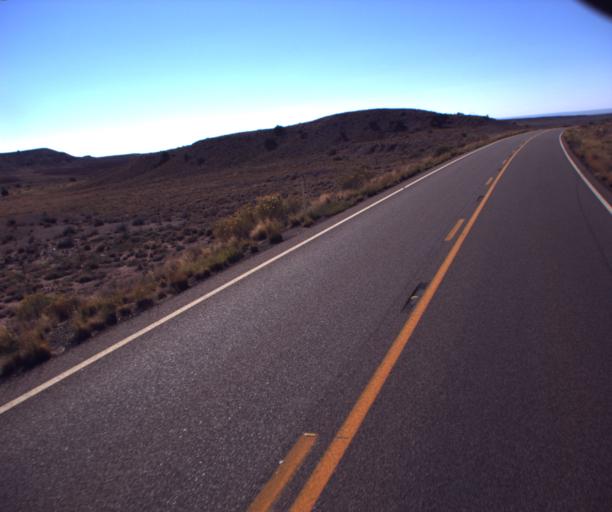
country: US
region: Arizona
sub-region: Navajo County
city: Dilkon
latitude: 35.1791
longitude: -110.4428
